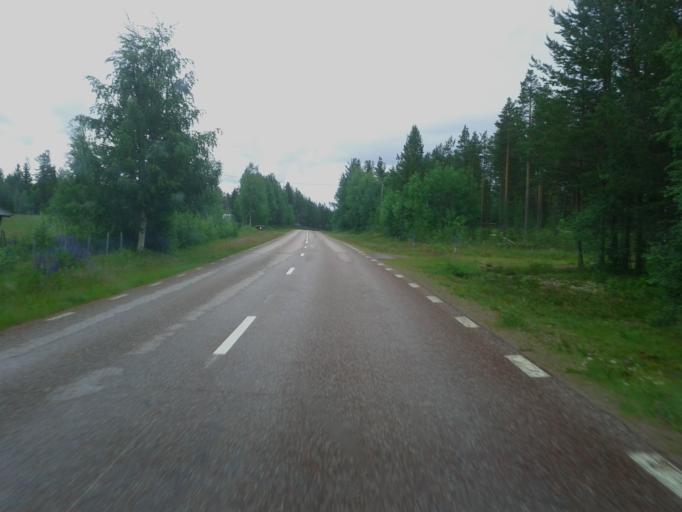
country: NO
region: Hedmark
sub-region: Trysil
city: Innbygda
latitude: 61.7240
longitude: 12.9953
